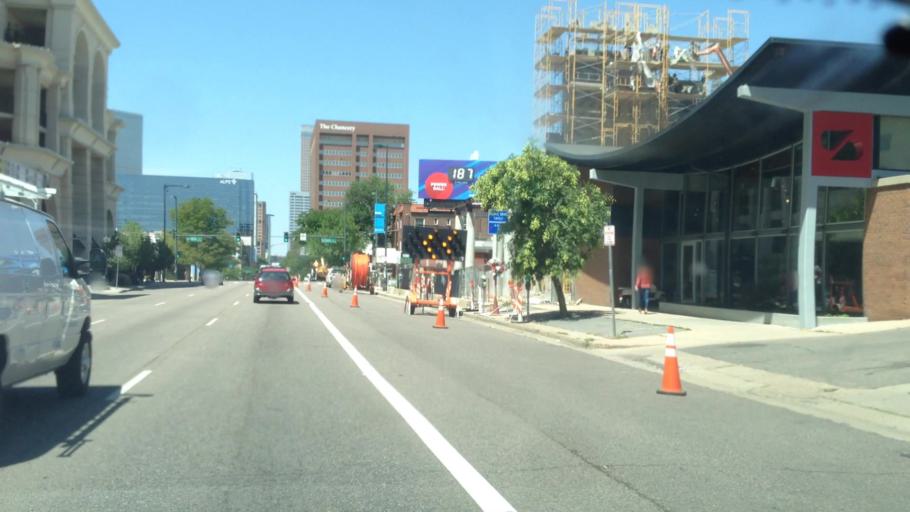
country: US
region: Colorado
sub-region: Denver County
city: Denver
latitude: 39.7310
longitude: -104.9861
